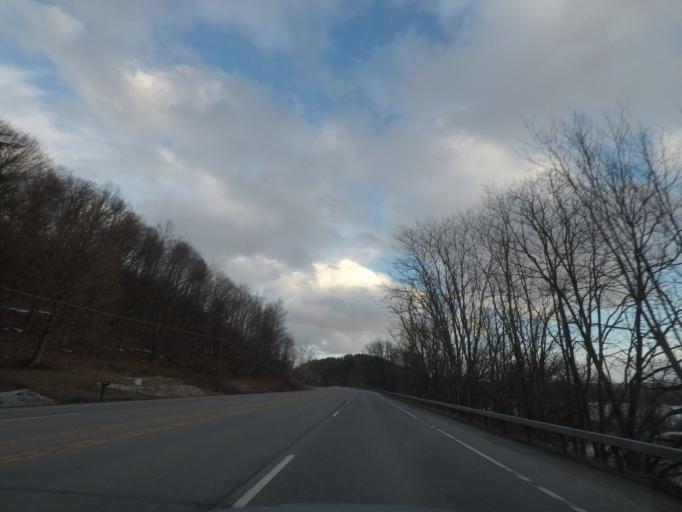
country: US
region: New York
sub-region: Herkimer County
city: Little Falls
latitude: 43.0274
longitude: -74.7934
